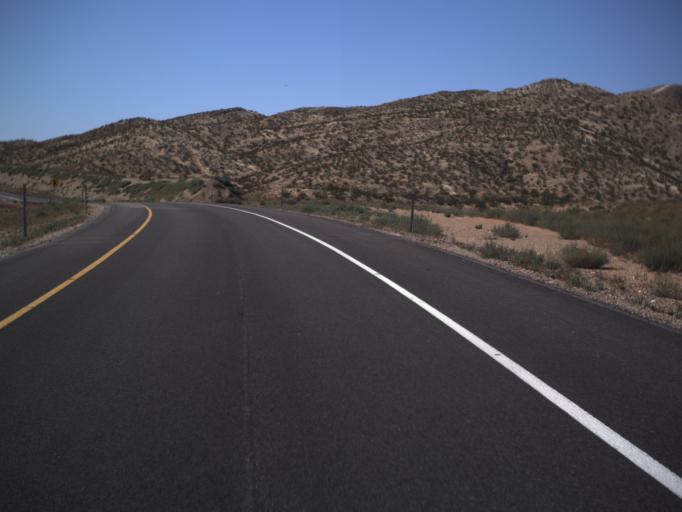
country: US
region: Utah
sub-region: Washington County
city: Washington
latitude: 37.1116
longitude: -113.4598
